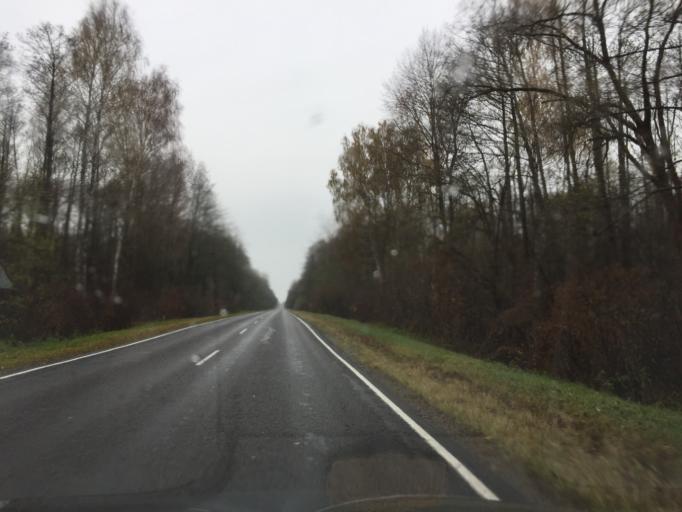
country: BY
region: Gomel
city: Karma
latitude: 53.3195
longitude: 30.7602
